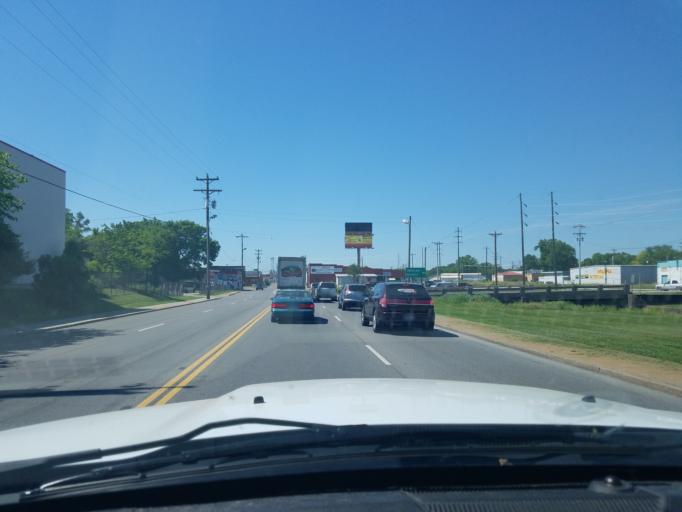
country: US
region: Tennessee
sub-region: Wilson County
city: Lebanon
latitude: 36.2056
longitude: -86.2915
